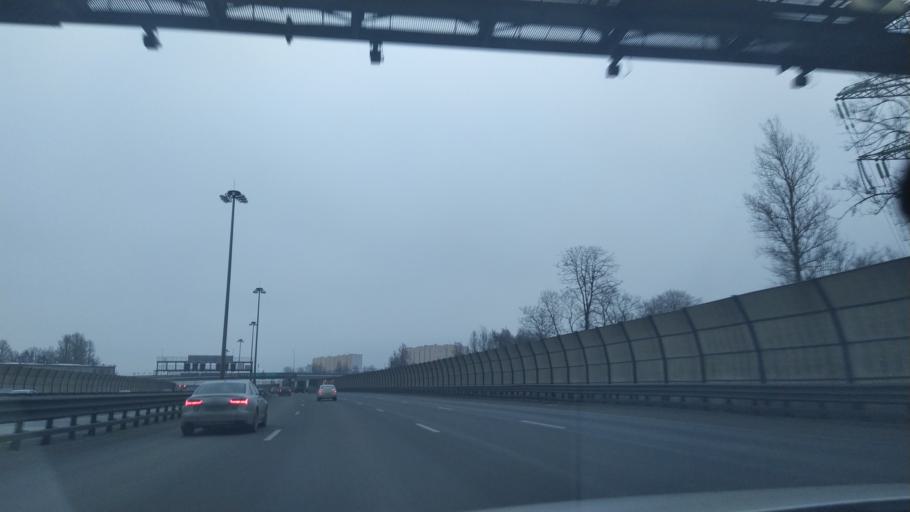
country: RU
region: St.-Petersburg
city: Krasnogvargeisky
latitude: 59.9840
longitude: 30.4966
